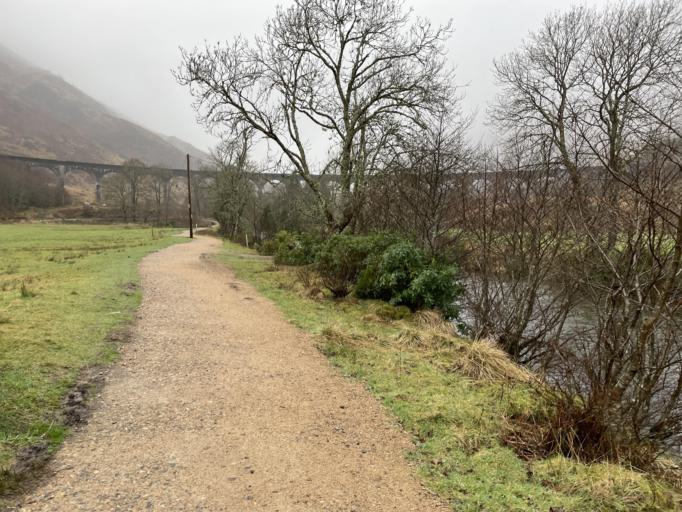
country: GB
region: Scotland
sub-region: Highland
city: Fort William
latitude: 56.8735
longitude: -5.4319
